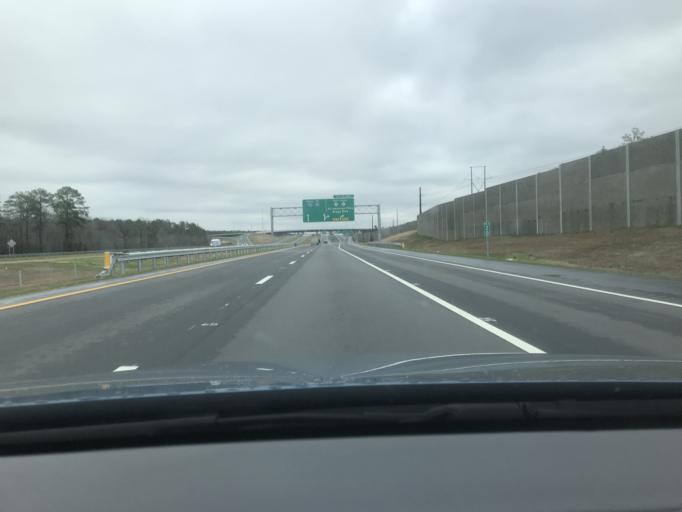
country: US
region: North Carolina
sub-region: Cumberland County
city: Fort Bragg
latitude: 35.1090
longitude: -78.9863
